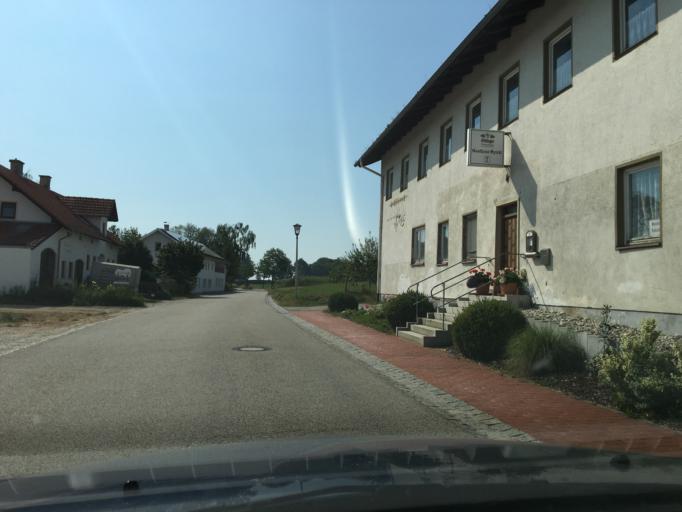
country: DE
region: Bavaria
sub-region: Upper Bavaria
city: Niederbergkirchen
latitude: 48.2988
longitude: 12.4856
